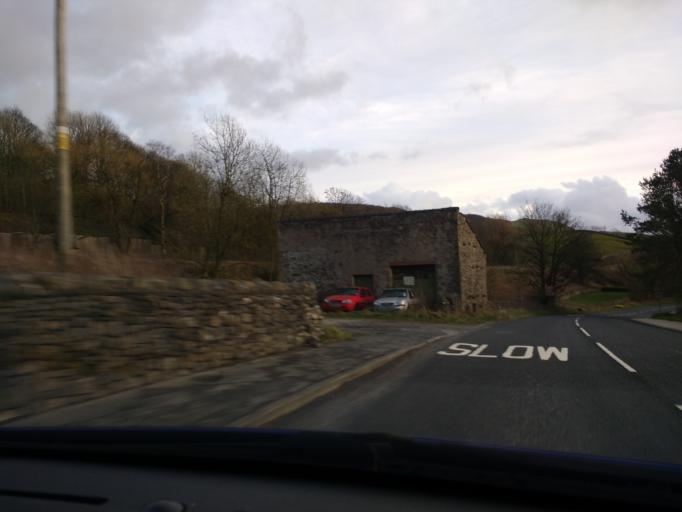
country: GB
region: England
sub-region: North Yorkshire
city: Settle
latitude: 54.0914
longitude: -2.2724
